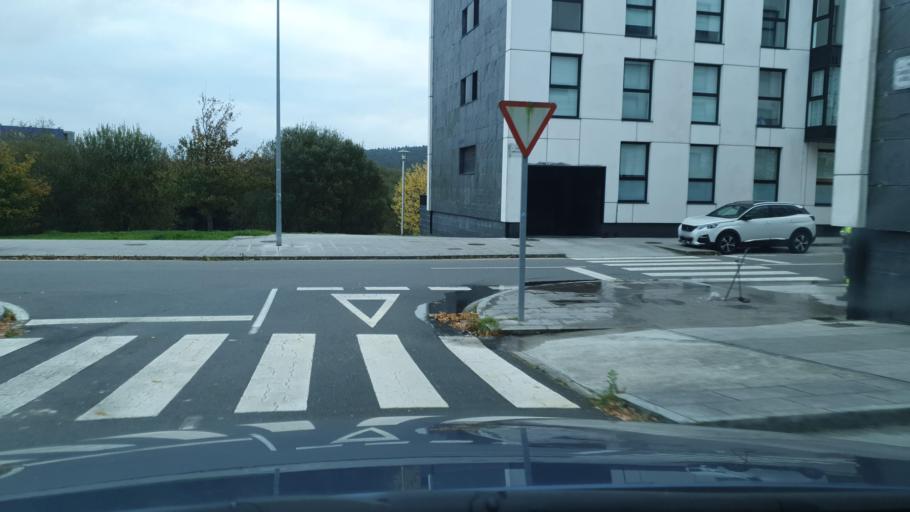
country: ES
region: Galicia
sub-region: Provincia da Coruna
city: Santiago de Compostela
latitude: 42.8656
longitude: -8.5635
